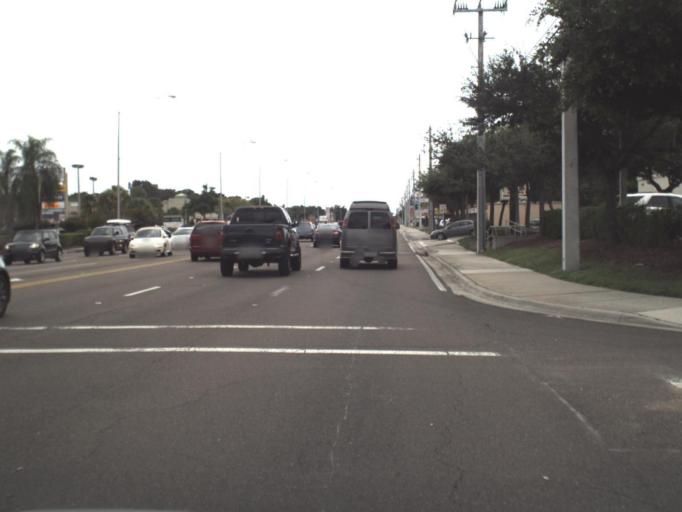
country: US
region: Florida
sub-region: Sarasota County
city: Sarasota Springs
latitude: 27.2988
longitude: -82.4810
